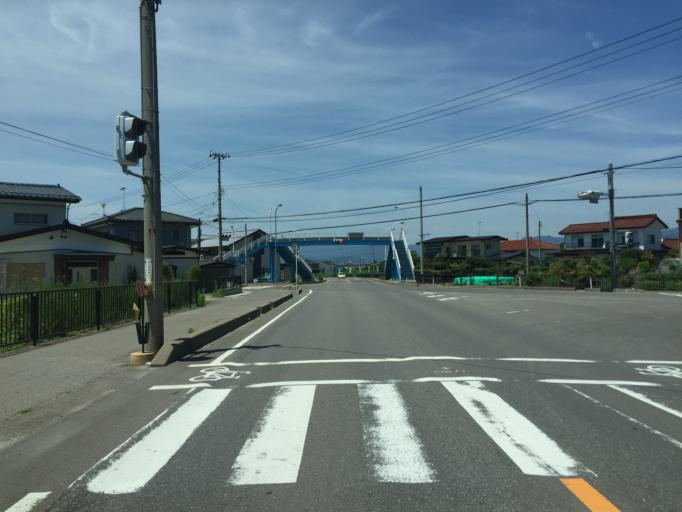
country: JP
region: Fukushima
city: Fukushima-shi
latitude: 37.7708
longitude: 140.5096
